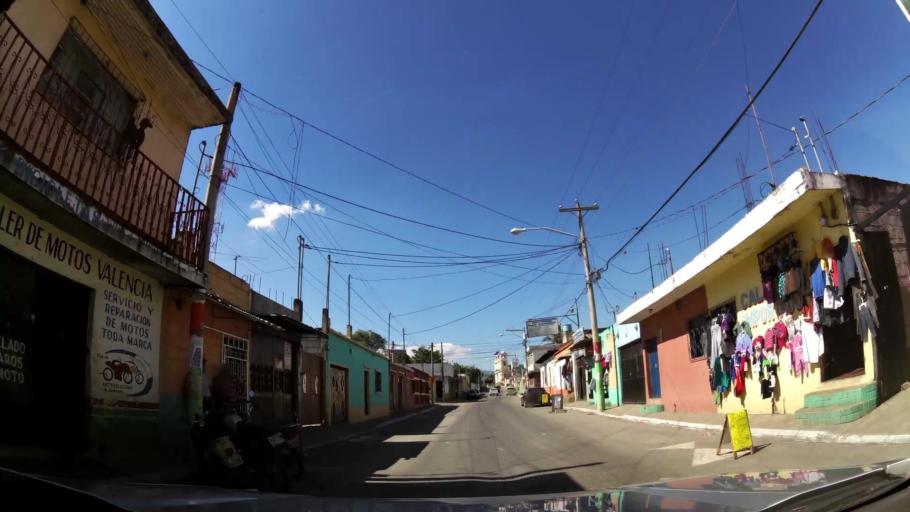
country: GT
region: Guatemala
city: Petapa
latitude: 14.5005
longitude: -90.5588
